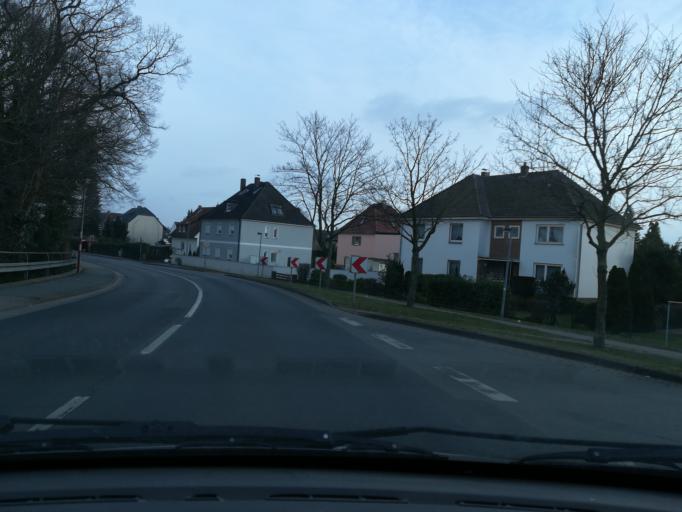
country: DE
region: Lower Saxony
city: Garbsen
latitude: 52.3978
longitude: 9.5710
